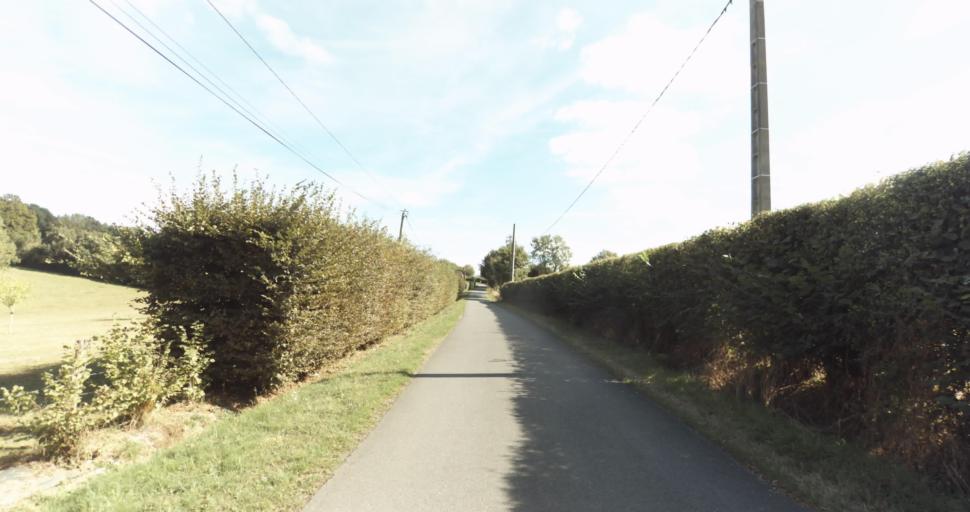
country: FR
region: Lower Normandy
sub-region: Departement de l'Orne
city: Vimoutiers
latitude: 48.9204
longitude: 0.1422
